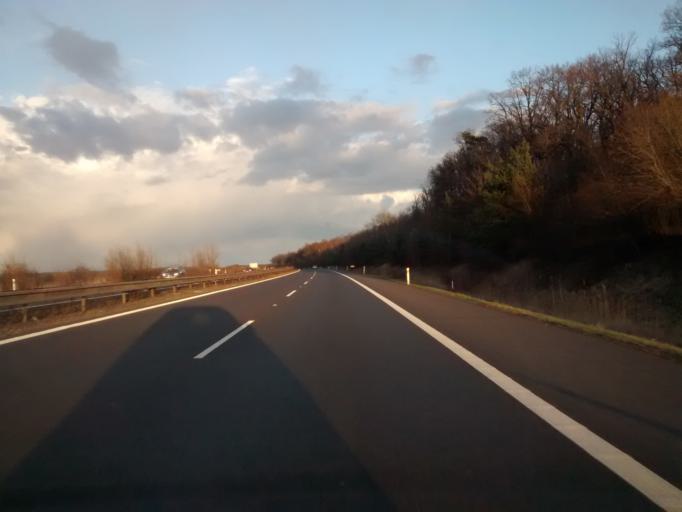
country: CZ
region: Central Bohemia
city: Poricany
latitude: 50.1299
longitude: 14.8720
